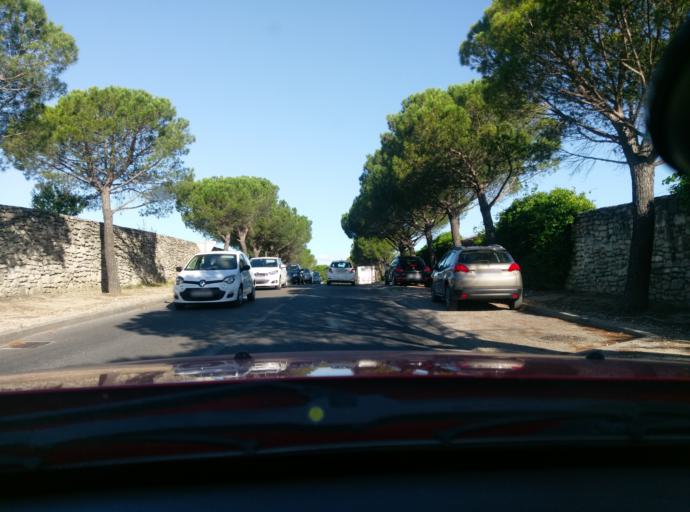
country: FR
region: Languedoc-Roussillon
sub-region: Departement du Gard
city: Uzes
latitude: 44.0071
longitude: 4.4169
